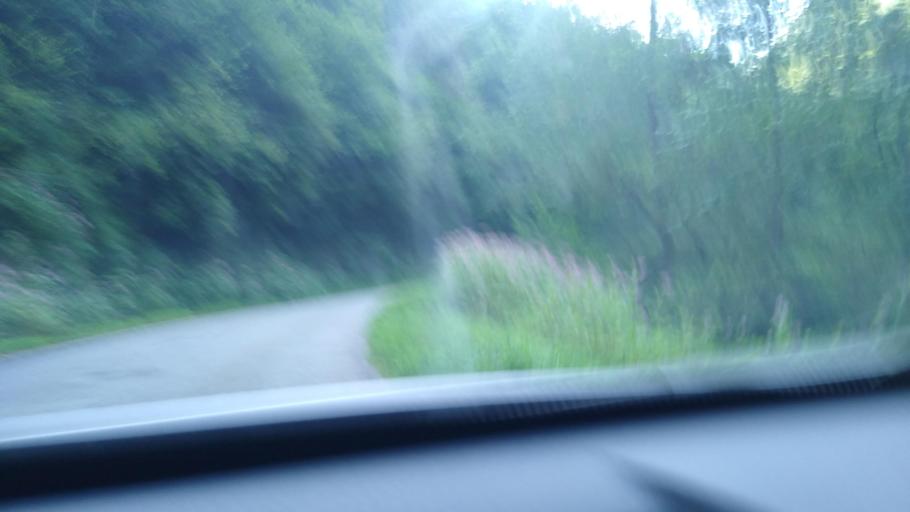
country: FR
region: Midi-Pyrenees
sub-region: Departement de l'Ariege
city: Saint-Girons
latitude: 42.8249
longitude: 1.1972
